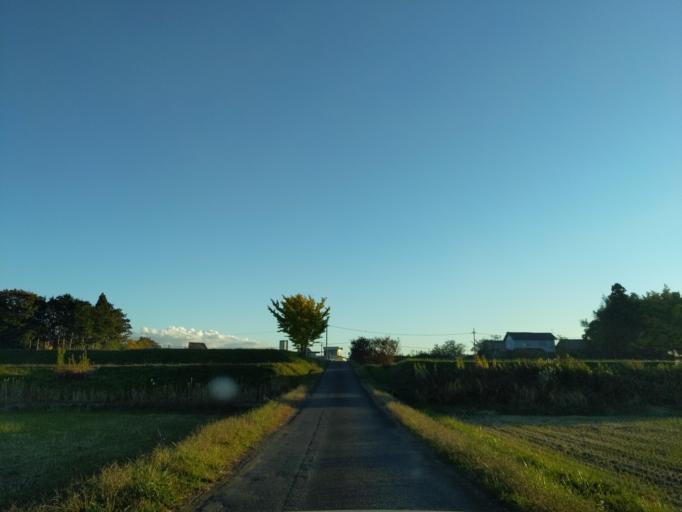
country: JP
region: Fukushima
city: Koriyama
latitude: 37.4455
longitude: 140.3734
